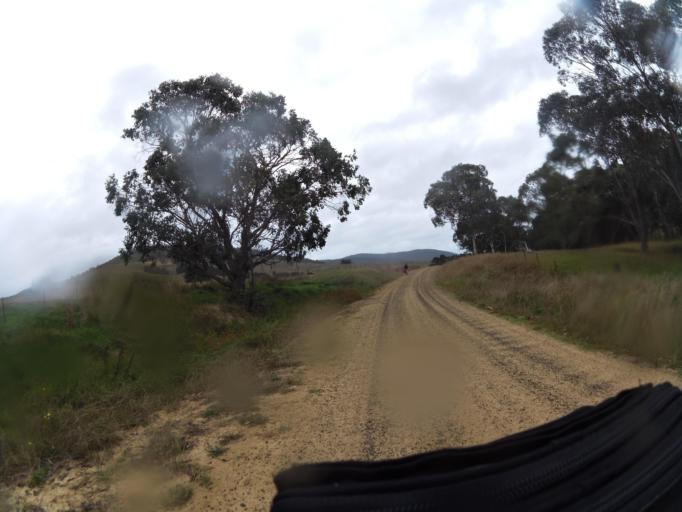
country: AU
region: New South Wales
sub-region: Greater Hume Shire
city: Holbrook
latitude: -36.2400
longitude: 147.6378
